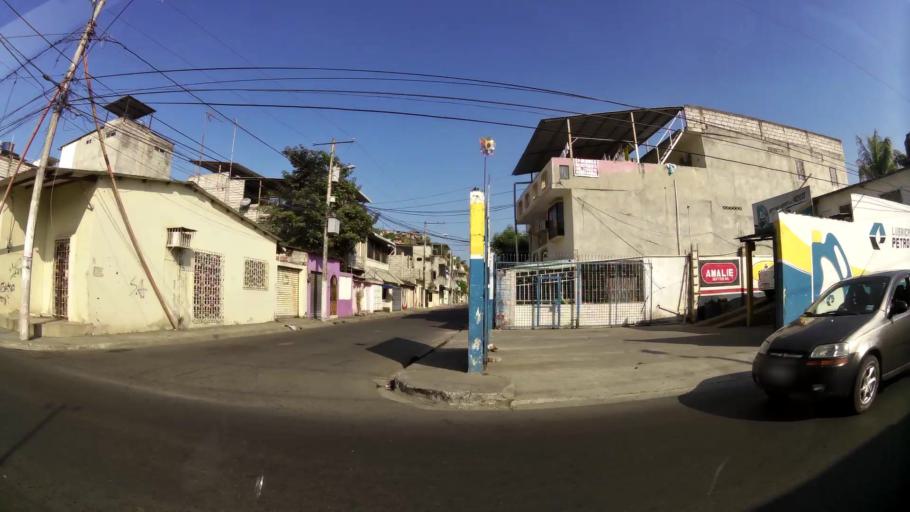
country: EC
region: Guayas
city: Eloy Alfaro
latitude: -2.1712
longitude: -79.8446
